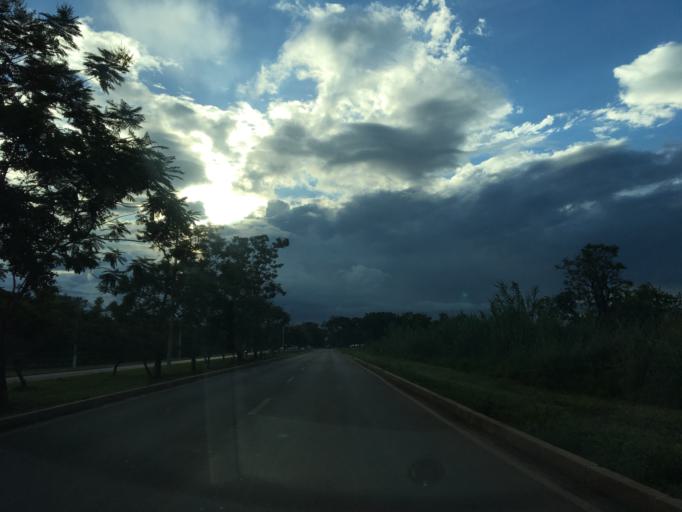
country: BR
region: Federal District
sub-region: Brasilia
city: Brasilia
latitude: -15.8147
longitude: -47.8533
